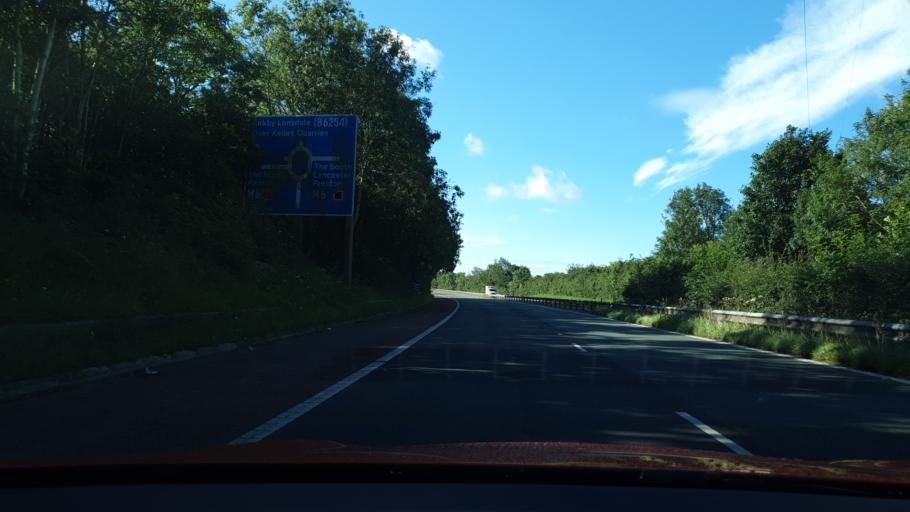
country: GB
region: England
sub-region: Lancashire
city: Carnforth
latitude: 54.1323
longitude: -2.7514
